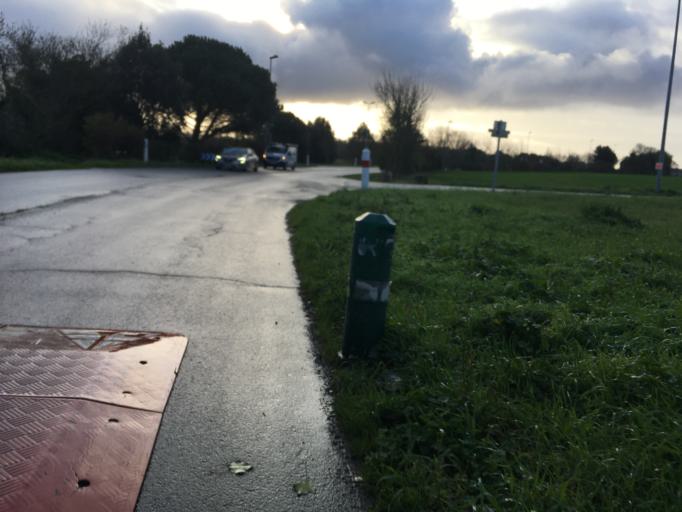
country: FR
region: Poitou-Charentes
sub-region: Departement de la Charente-Maritime
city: Nieul-sur-Mer
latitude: 46.1896
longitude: -1.1825
